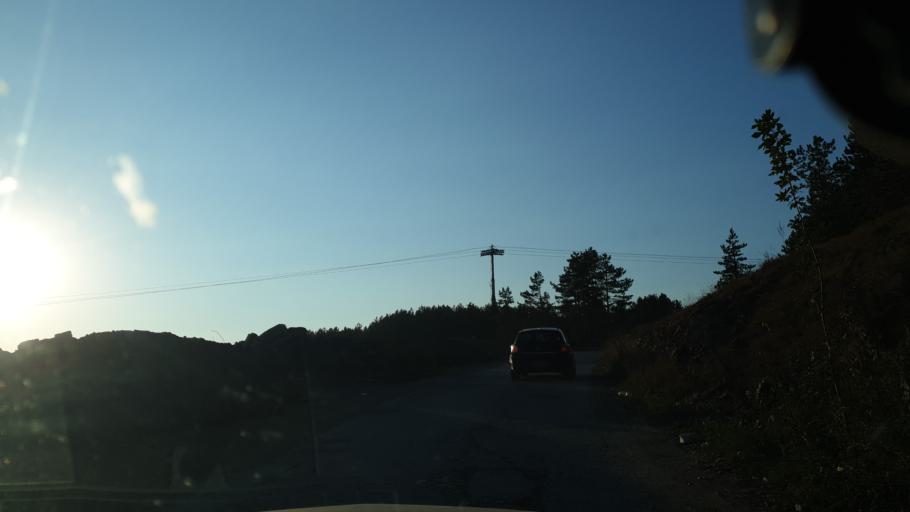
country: RS
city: Zlatibor
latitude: 43.7186
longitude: 19.6945
